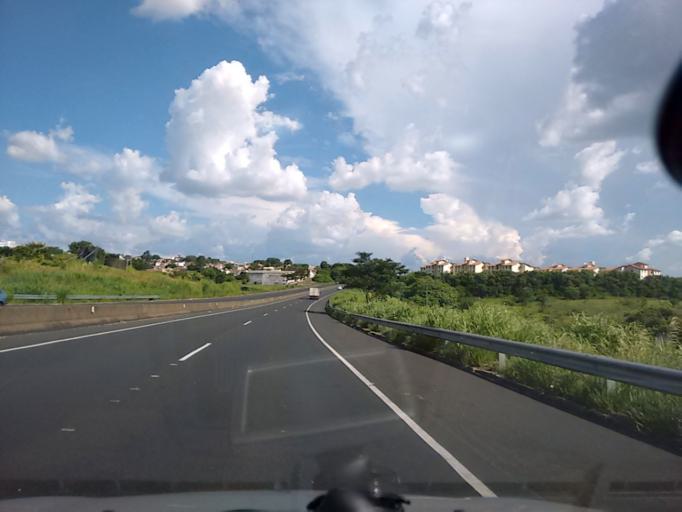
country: BR
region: Sao Paulo
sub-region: Marilia
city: Marilia
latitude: -22.1902
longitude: -49.9673
